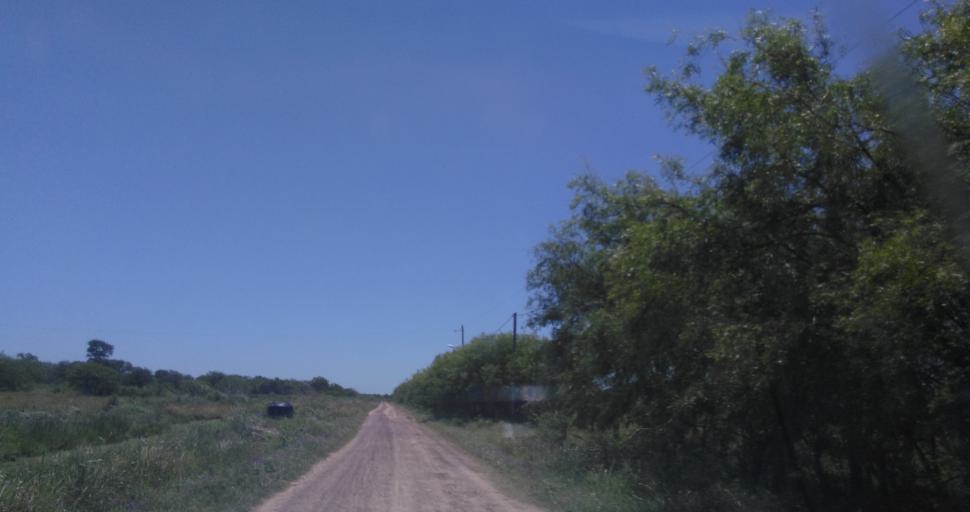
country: AR
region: Chaco
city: Fontana
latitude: -27.4864
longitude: -59.0573
